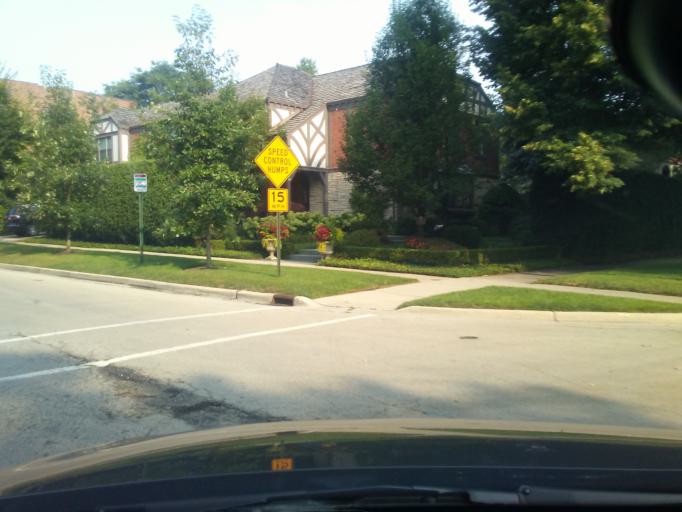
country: US
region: Illinois
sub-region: Cook County
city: Evanston
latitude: 42.0392
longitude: -87.6722
